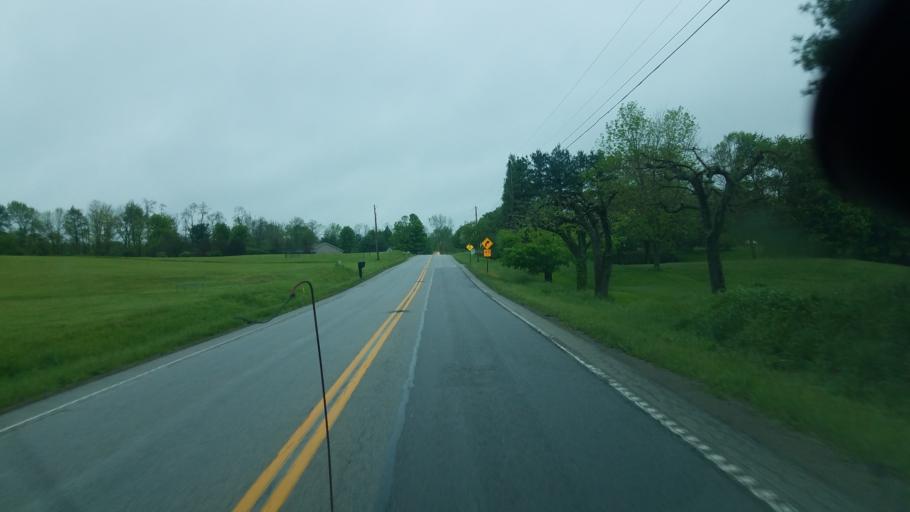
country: US
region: Ohio
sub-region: Highland County
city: Hillsboro
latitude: 39.2551
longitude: -83.6012
